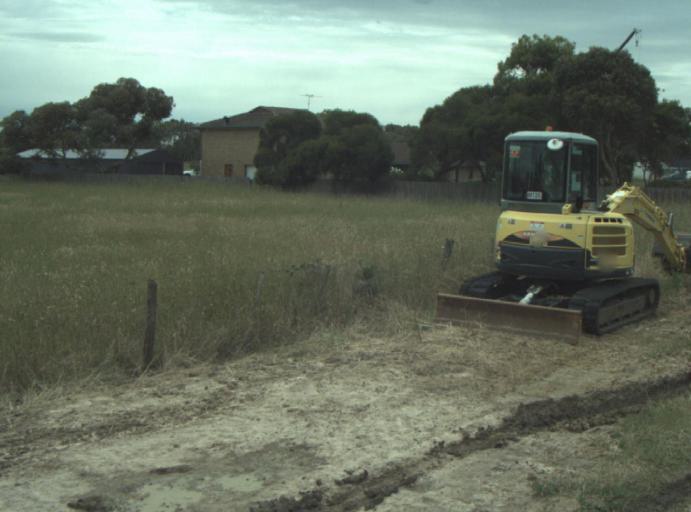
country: AU
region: Victoria
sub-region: Greater Geelong
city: Leopold
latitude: -38.1796
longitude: 144.4570
